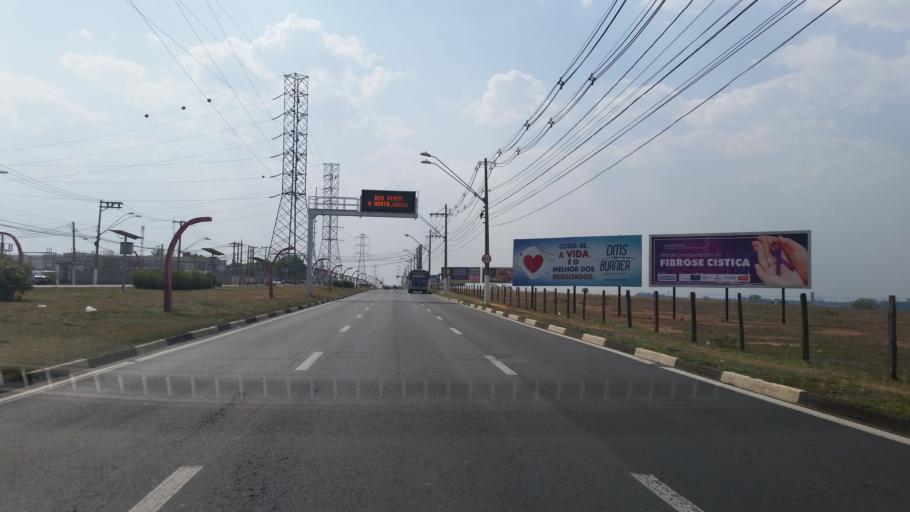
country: BR
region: Sao Paulo
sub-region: Hortolandia
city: Hortolandia
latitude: -22.8920
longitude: -47.1905
